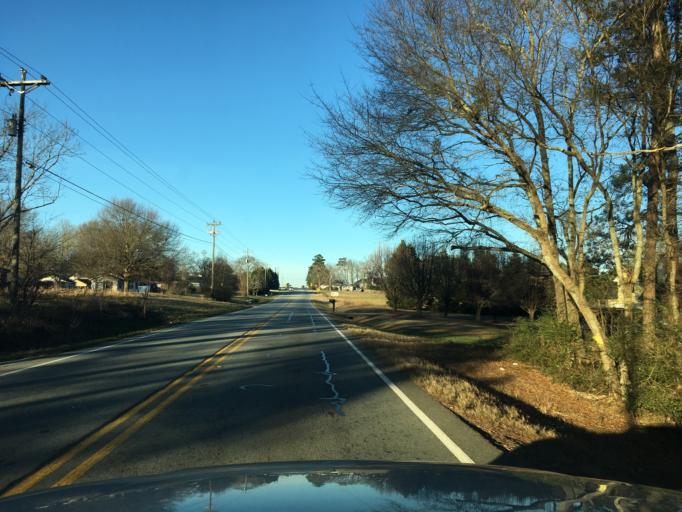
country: US
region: Georgia
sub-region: Barrow County
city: Winder
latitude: 33.9335
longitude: -83.7657
